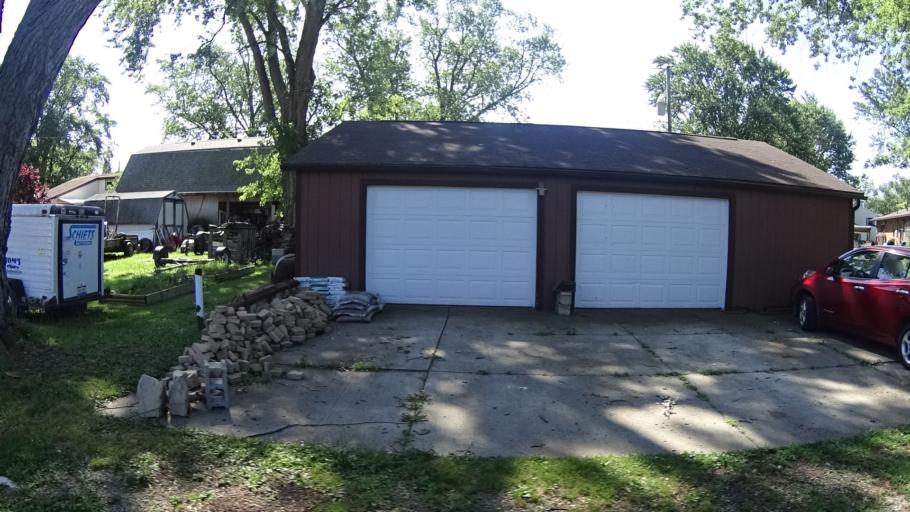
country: US
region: Ohio
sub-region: Erie County
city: Sandusky
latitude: 41.4685
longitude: -82.8253
